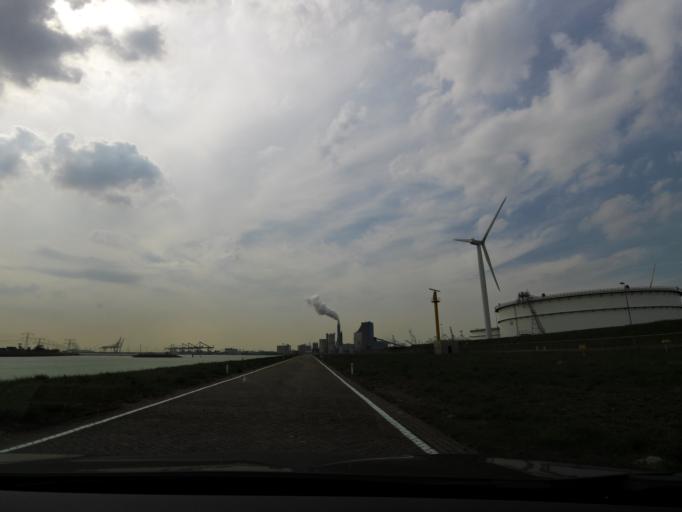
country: NL
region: South Holland
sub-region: Gemeente Rotterdam
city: Hoek van Holland
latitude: 51.9404
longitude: 4.0899
